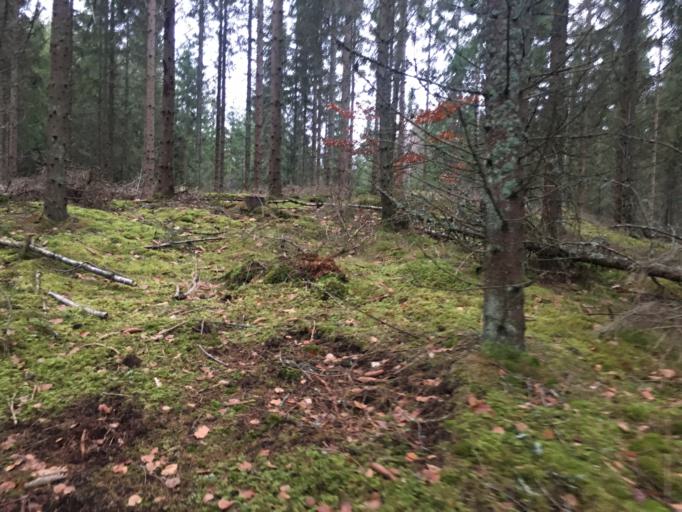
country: SE
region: Joenkoeping
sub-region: Varnamo Kommun
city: Bor
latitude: 57.0372
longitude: 14.1950
